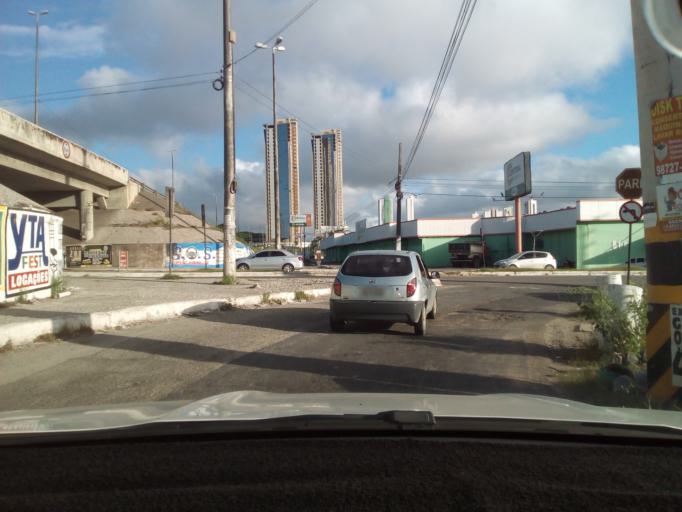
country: BR
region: Paraiba
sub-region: Joao Pessoa
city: Joao Pessoa
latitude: -7.0979
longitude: -34.8481
